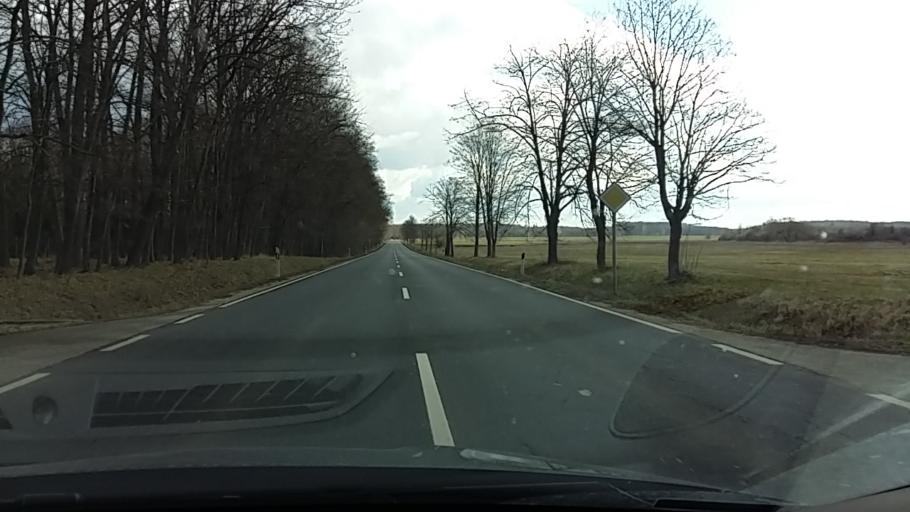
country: HU
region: Somogy
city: Bohonye
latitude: 46.4089
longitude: 17.4136
